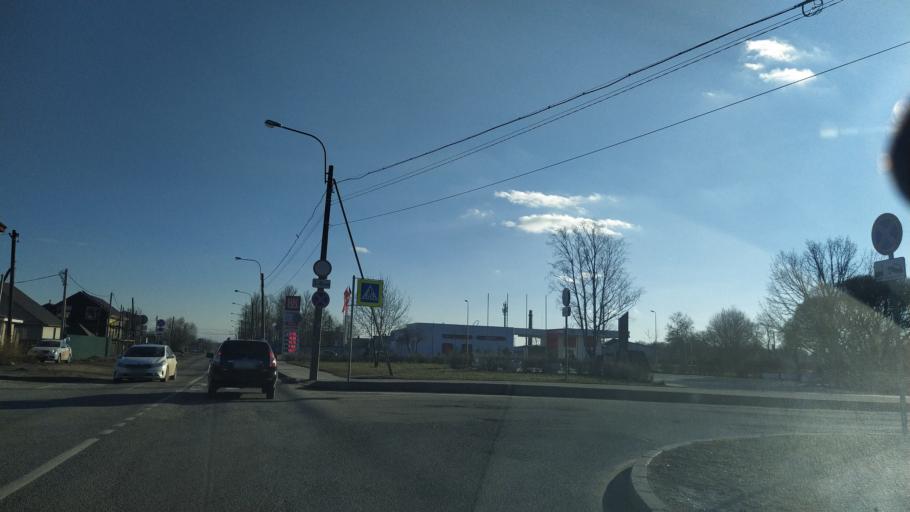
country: RU
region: St.-Petersburg
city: Pushkin
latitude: 59.7003
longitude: 30.3943
